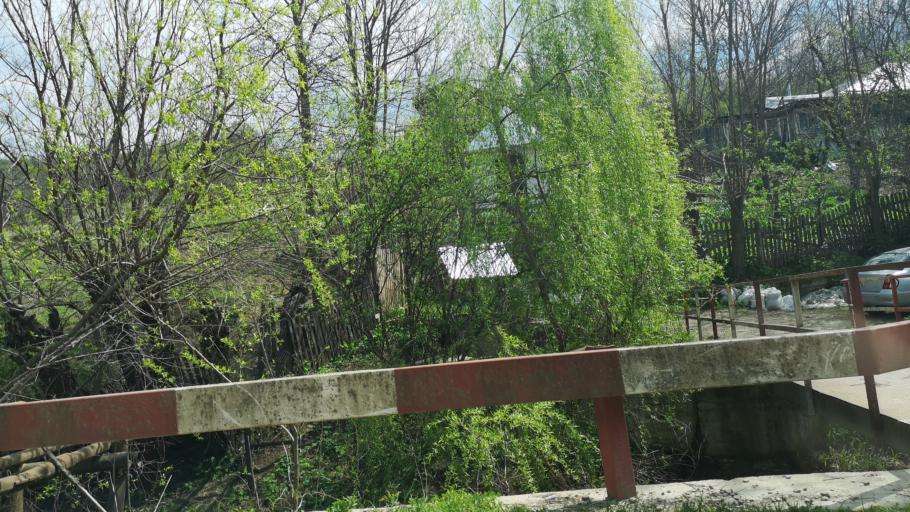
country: RO
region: Prahova
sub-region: Comuna Soimari
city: Soimari
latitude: 45.1794
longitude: 26.2172
